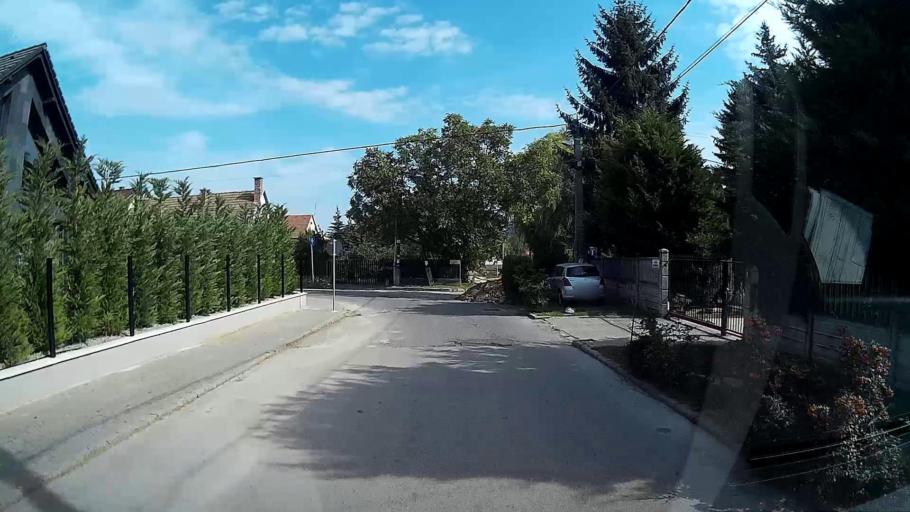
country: HU
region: Pest
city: Solymar
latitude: 47.5896
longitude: 18.9307
